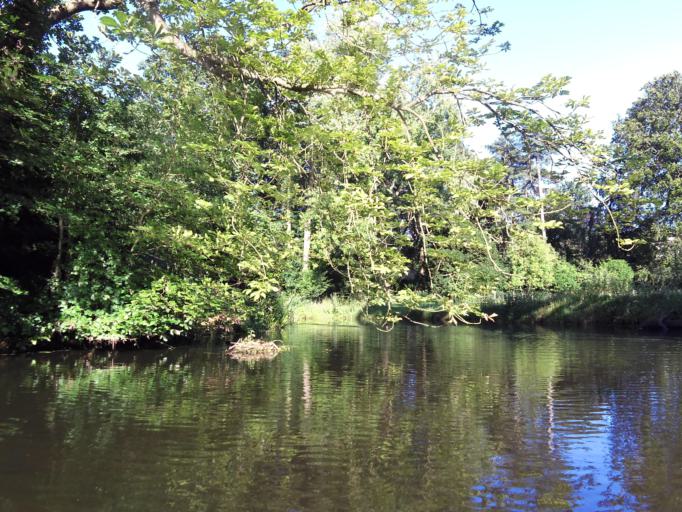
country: NL
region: South Holland
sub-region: Gemeente Wassenaar
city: Wassenaar
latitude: 52.1237
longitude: 4.3776
